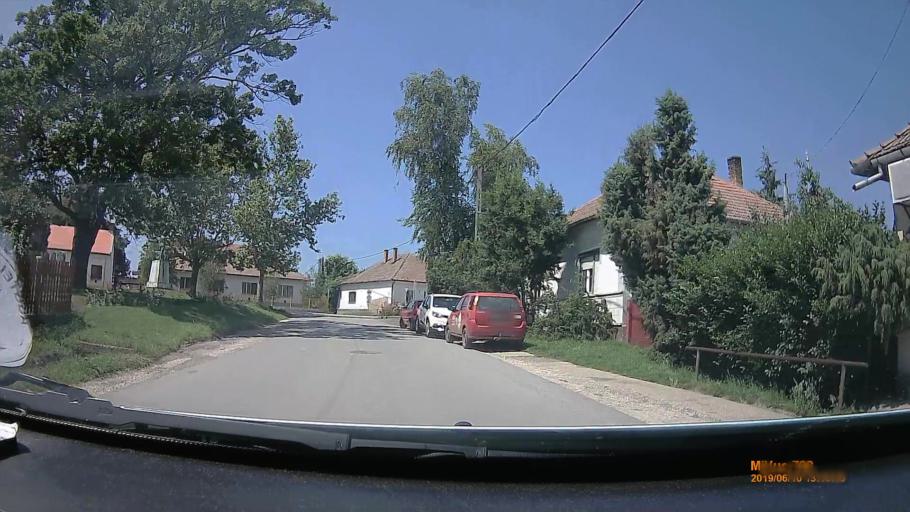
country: HU
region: Szabolcs-Szatmar-Bereg
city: Tiszadob
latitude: 48.0127
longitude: 21.1673
